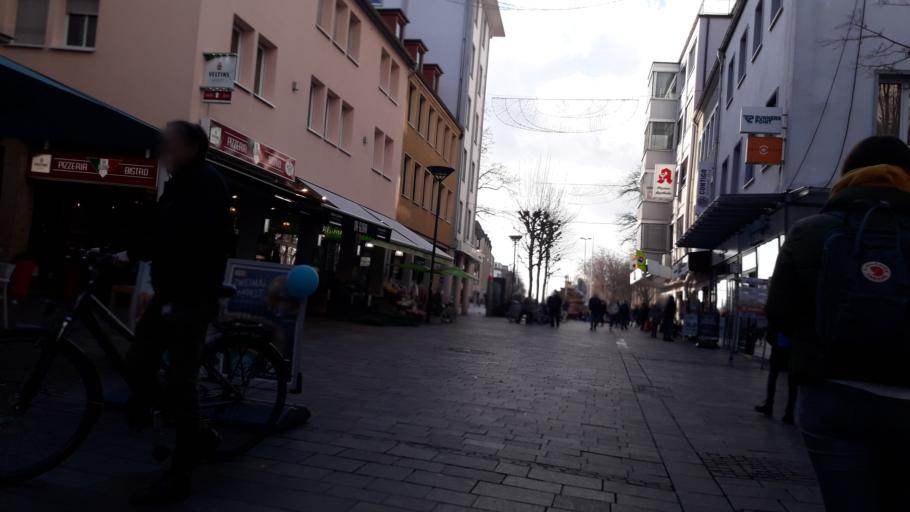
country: DE
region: North Rhine-Westphalia
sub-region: Regierungsbezirk Detmold
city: Paderborn
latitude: 51.7160
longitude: 8.7477
